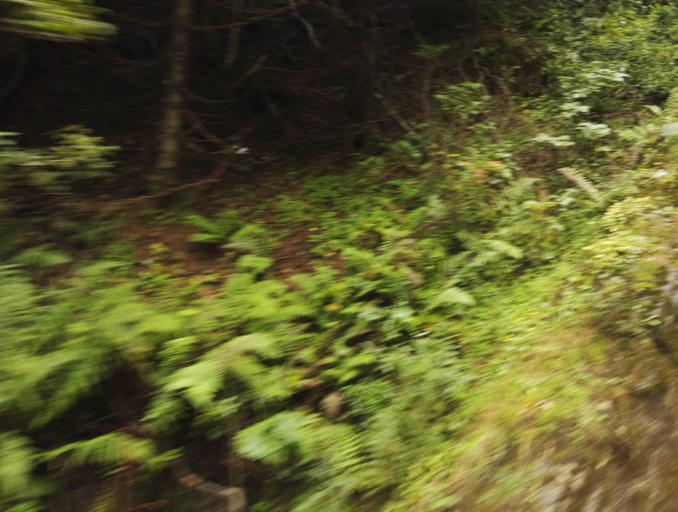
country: AT
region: Styria
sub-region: Politischer Bezirk Leoben
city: Eisenerz
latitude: 47.5262
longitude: 14.9445
